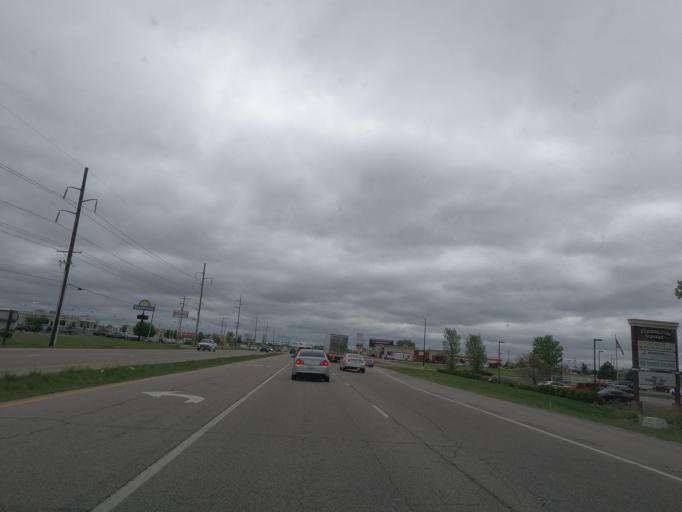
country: US
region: Kansas
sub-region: Butler County
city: Andover
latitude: 37.6796
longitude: -97.1387
